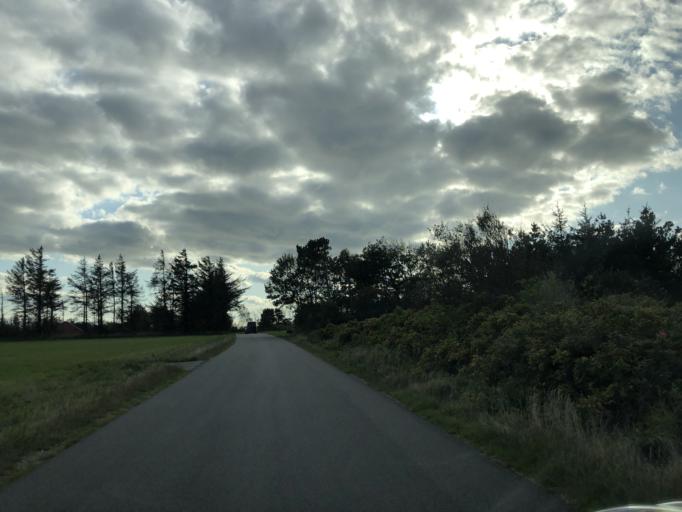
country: DK
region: Central Jutland
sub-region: Holstebro Kommune
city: Ulfborg
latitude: 56.3268
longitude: 8.1582
